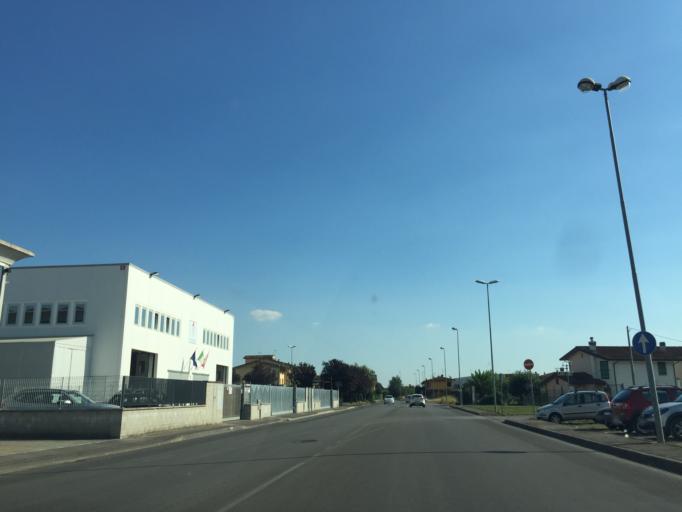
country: IT
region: Tuscany
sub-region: Provincia di Pistoia
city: Monsummano Terme
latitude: 43.8619
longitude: 10.8042
